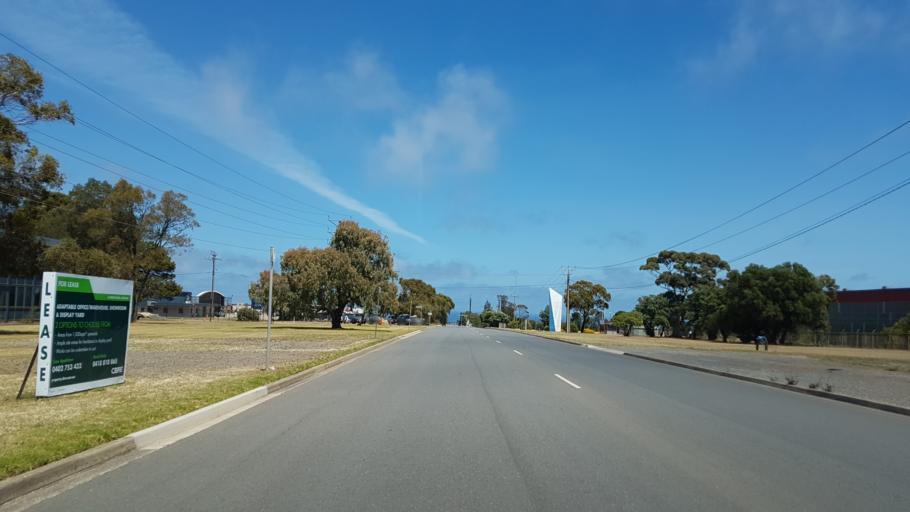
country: AU
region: South Australia
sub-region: Onkaparinga
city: Morphett Vale
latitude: -35.1067
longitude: 138.4940
